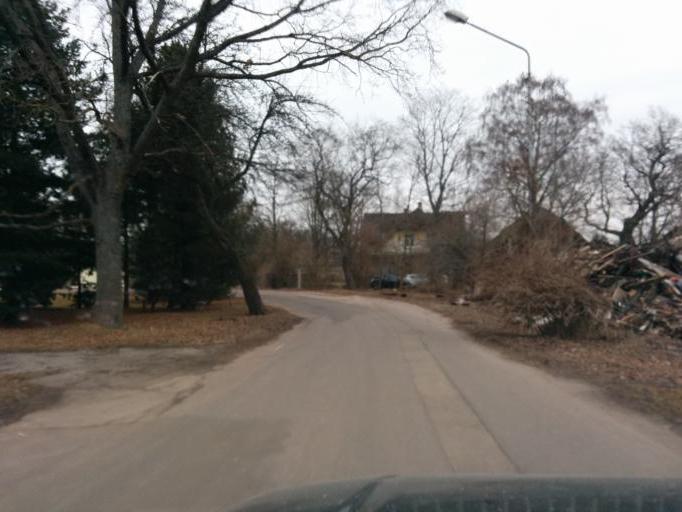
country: LV
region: Babite
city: Pinki
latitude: 56.9724
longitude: 23.8536
